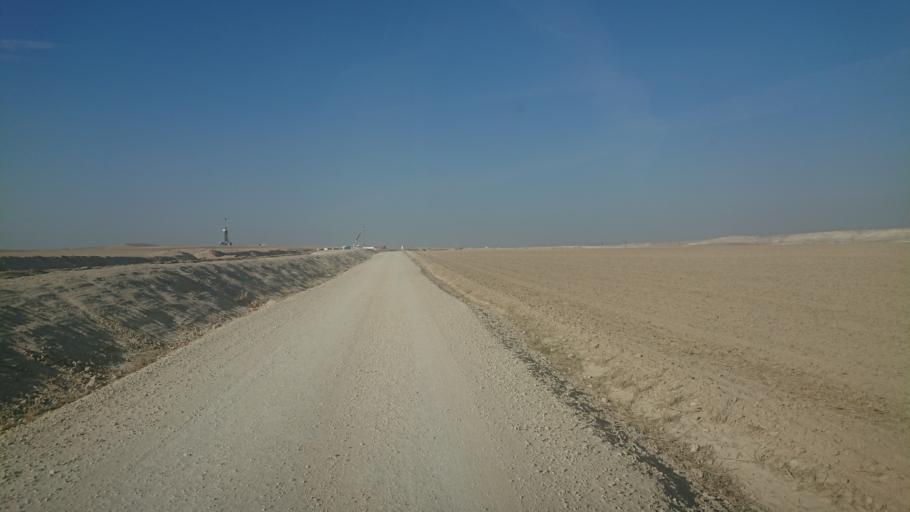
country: TR
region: Aksaray
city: Sultanhani
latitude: 38.0693
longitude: 33.6147
